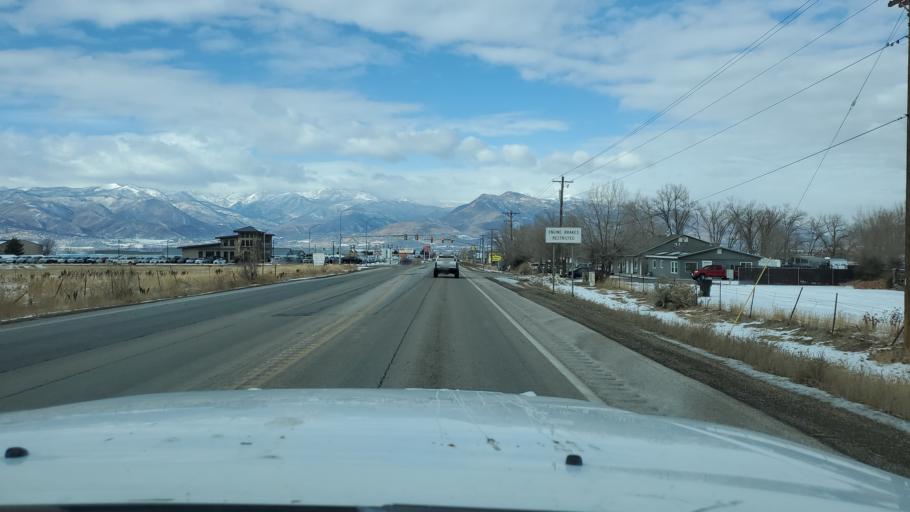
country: US
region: Utah
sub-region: Wasatch County
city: Heber
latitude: 40.4836
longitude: -111.4037
